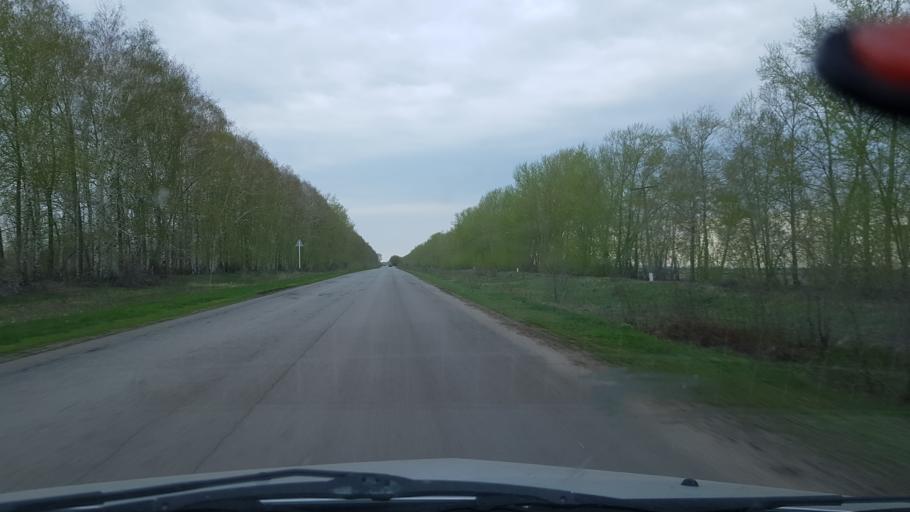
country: RU
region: Samara
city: Podstepki
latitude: 53.6638
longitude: 49.1863
